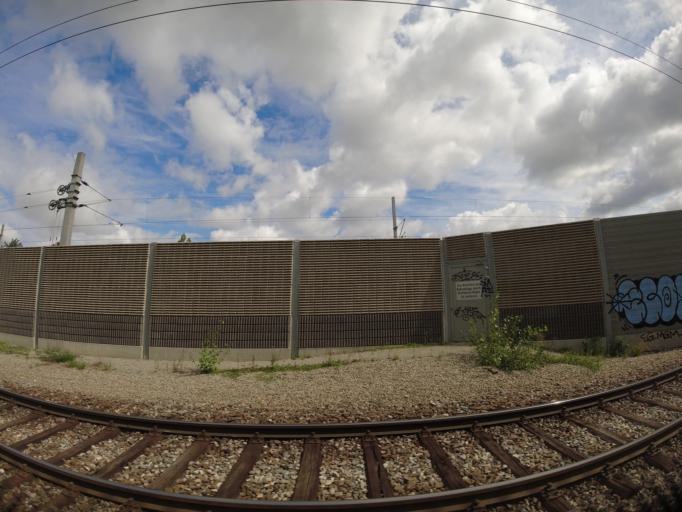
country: AT
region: Lower Austria
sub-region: Politischer Bezirk Modling
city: Vosendorf
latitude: 48.1624
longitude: 16.3331
